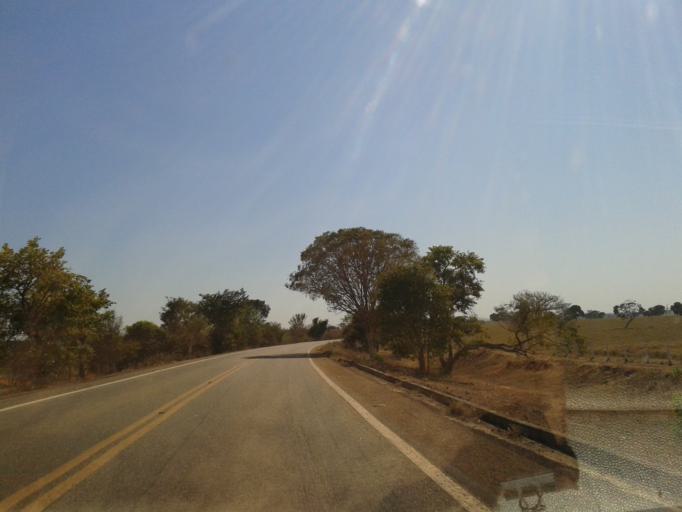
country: BR
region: Goias
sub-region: Crixas
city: Crixas
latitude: -14.2040
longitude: -50.3901
